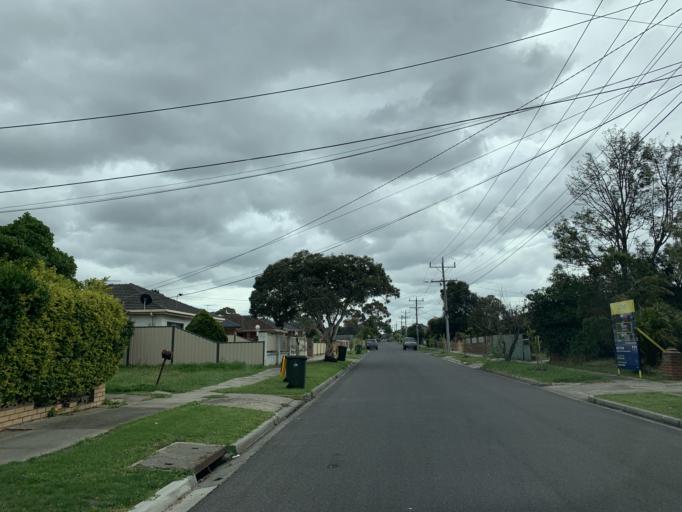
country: AU
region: Victoria
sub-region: Brimbank
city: Kealba
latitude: -37.7450
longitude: 144.8217
